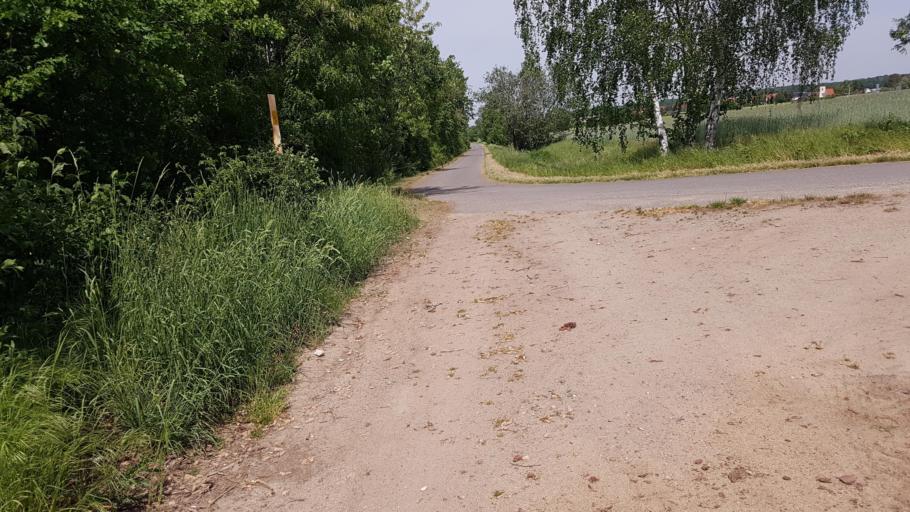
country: DE
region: Brandenburg
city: Grosskmehlen
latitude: 51.3774
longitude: 13.7087
